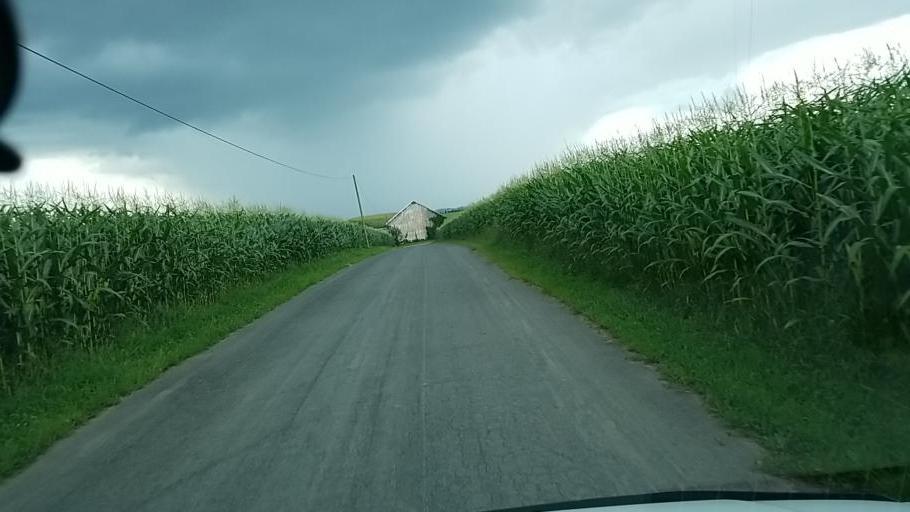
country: US
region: Pennsylvania
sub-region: Dauphin County
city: Elizabethville
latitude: 40.5794
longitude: -76.8573
